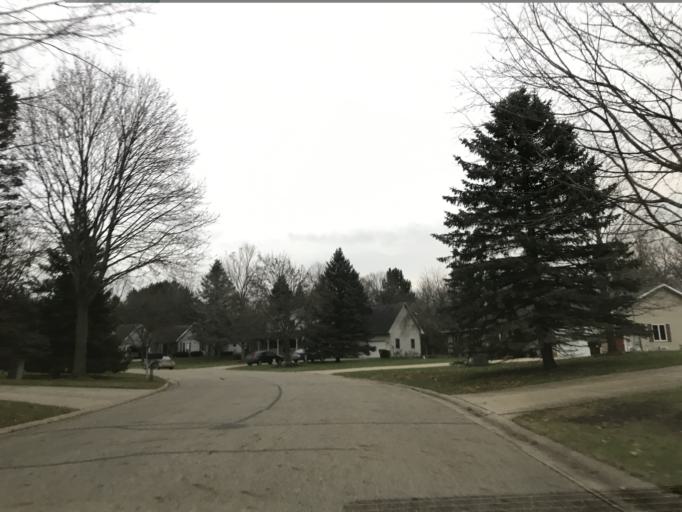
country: US
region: Michigan
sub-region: Eaton County
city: Dimondale
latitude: 42.6544
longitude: -84.6399
